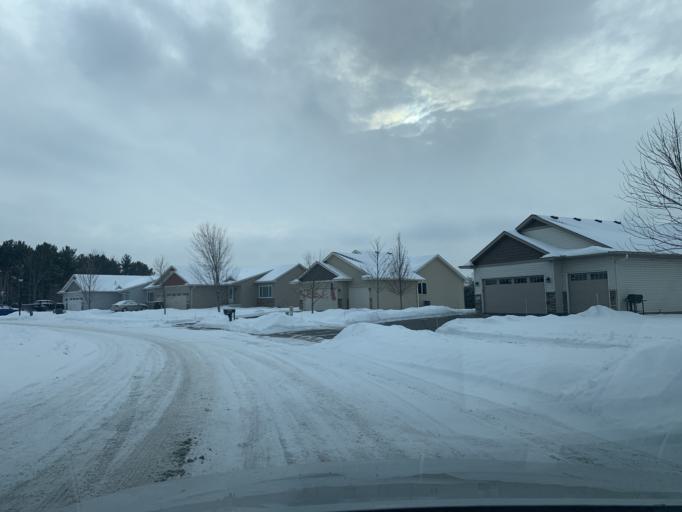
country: US
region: Minnesota
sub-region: Anoka County
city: Ramsey
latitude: 45.2475
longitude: -93.4146
